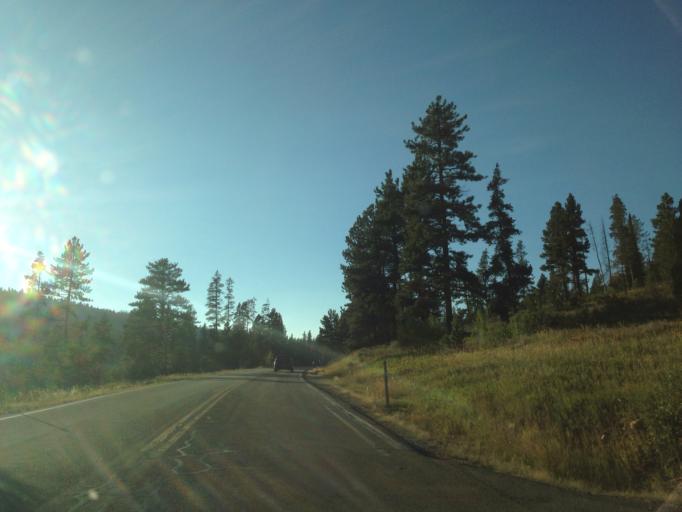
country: US
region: Utah
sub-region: Summit County
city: Francis
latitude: 40.6024
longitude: -111.1162
